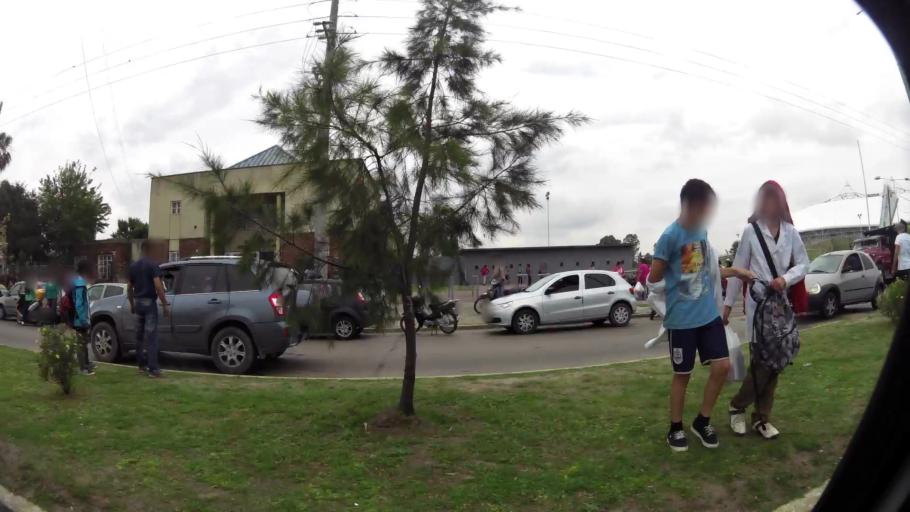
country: AR
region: Buenos Aires
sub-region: Partido de La Plata
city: La Plata
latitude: -34.9131
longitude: -57.9932
